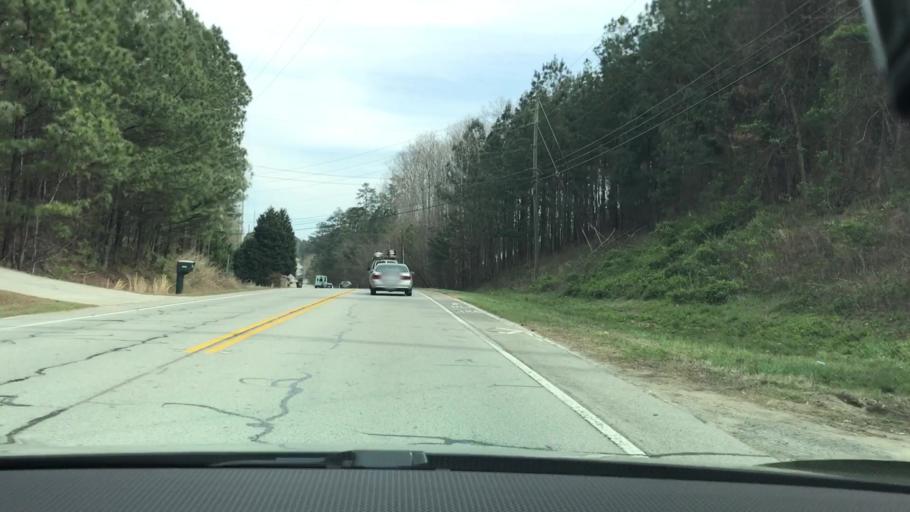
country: US
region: Georgia
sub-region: Gwinnett County
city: Sugar Hill
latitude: 34.1497
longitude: -84.0383
